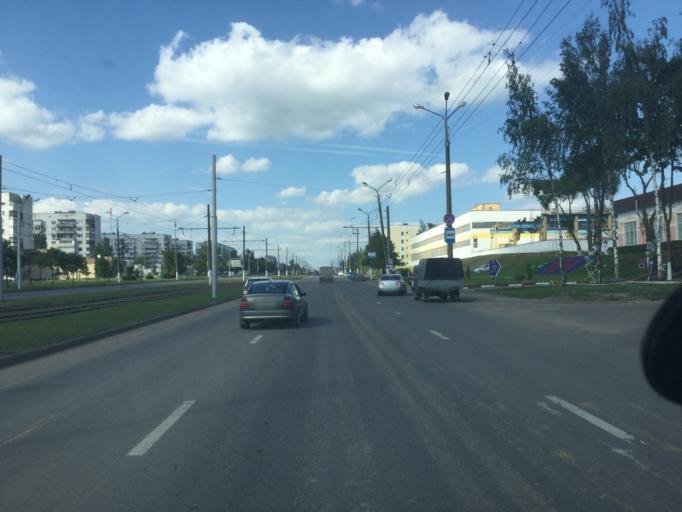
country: BY
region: Vitebsk
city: Vitebsk
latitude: 55.1690
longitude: 30.2422
